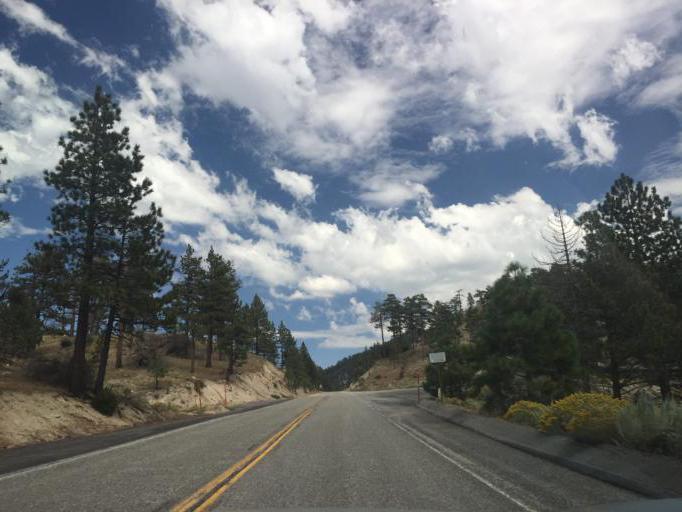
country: US
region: California
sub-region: Los Angeles County
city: Littlerock
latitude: 34.3491
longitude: -117.9642
